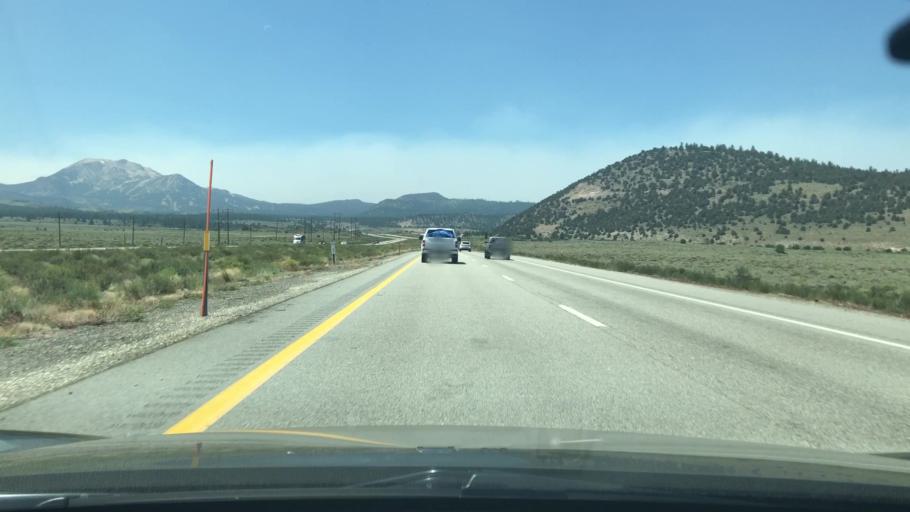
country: US
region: California
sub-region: Mono County
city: Mammoth Lakes
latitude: 37.6336
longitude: -118.8770
